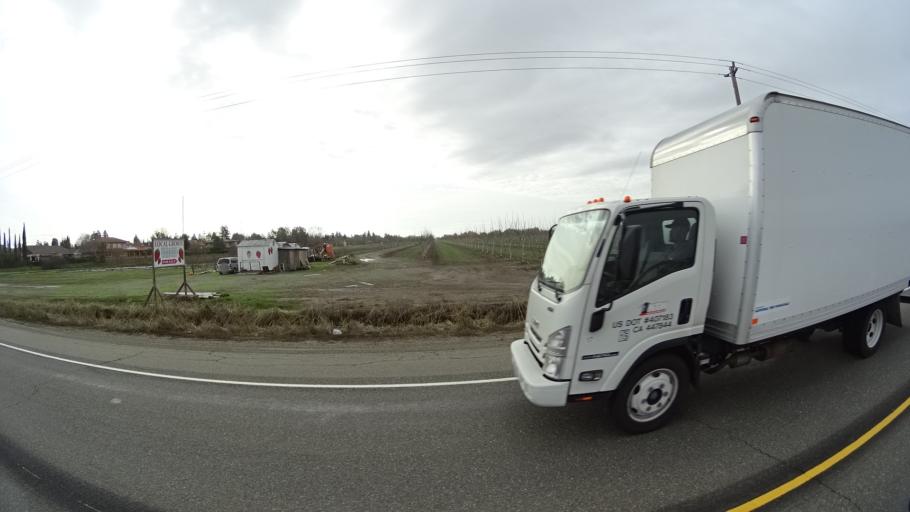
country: US
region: California
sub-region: Yolo County
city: Davis
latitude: 38.5614
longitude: -121.7951
